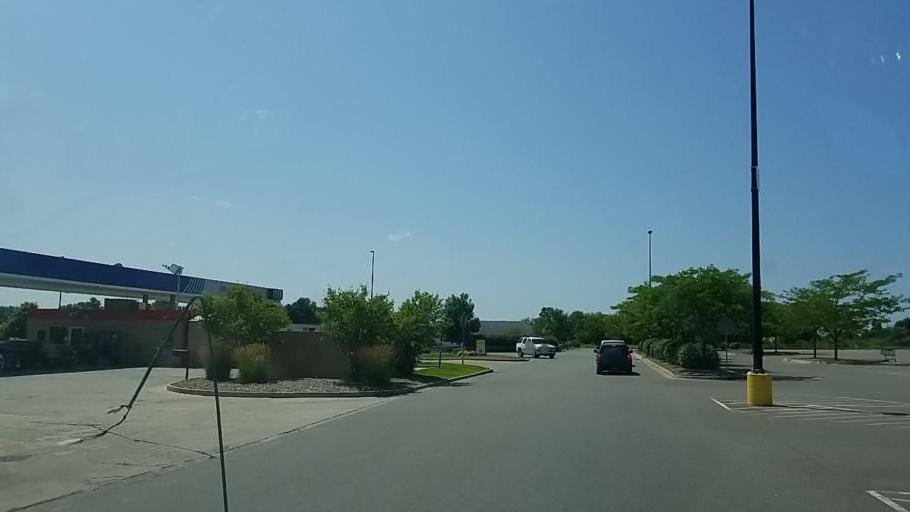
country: US
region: Michigan
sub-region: Newaygo County
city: Fremont
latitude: 43.4683
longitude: -85.9761
